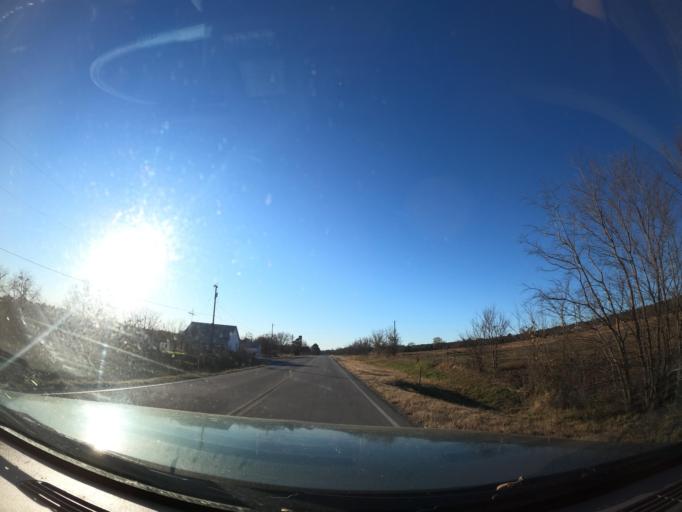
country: US
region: Oklahoma
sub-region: Pittsburg County
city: Hartshorne
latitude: 34.8876
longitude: -95.4681
